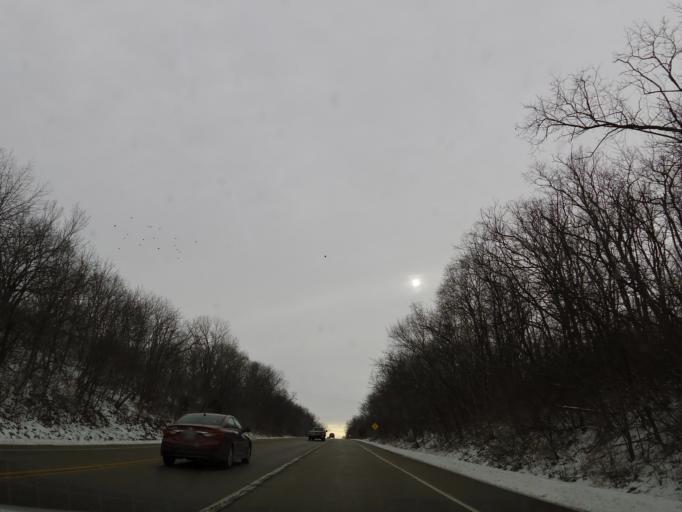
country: US
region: Illinois
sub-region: LaSalle County
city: Peru
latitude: 41.3075
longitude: -89.1133
